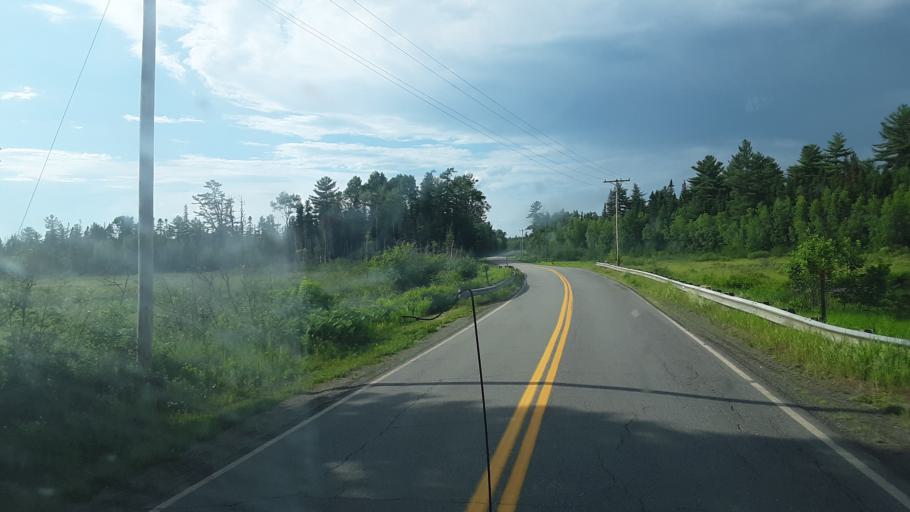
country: US
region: Maine
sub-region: Washington County
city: Calais
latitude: 45.1780
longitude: -67.5153
